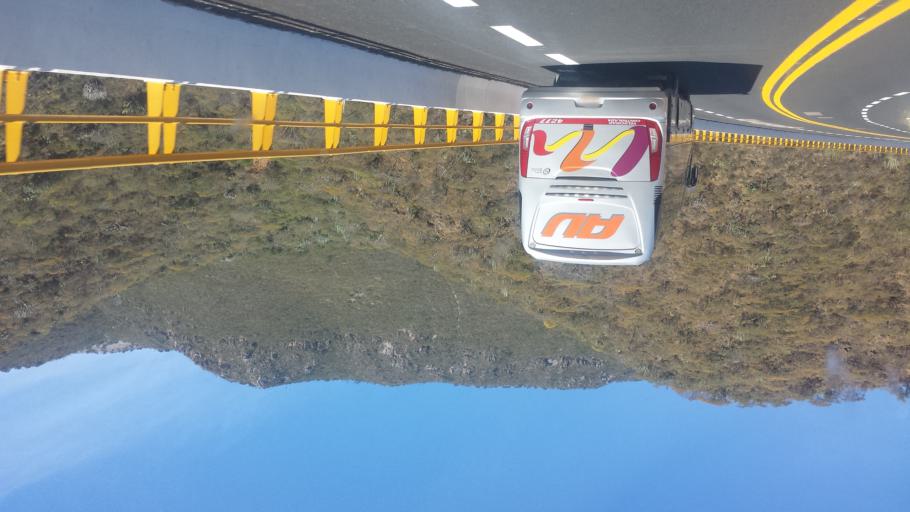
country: MX
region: Puebla
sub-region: San Jose Miahuatlan
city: San Pedro Tetitlan
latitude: 18.0907
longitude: -97.3400
